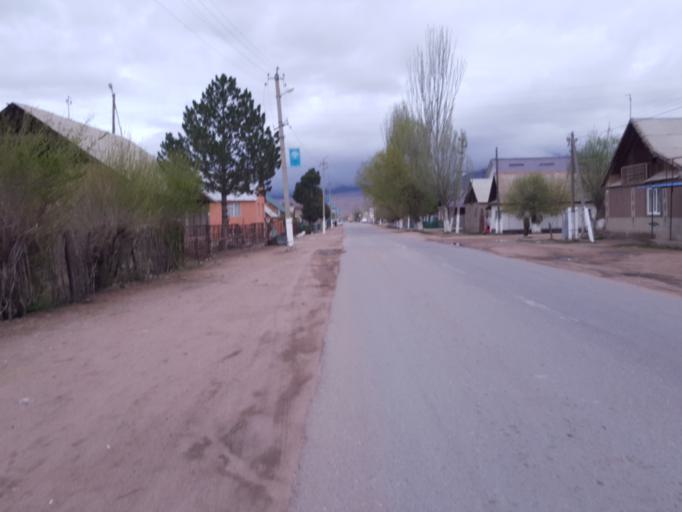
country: KG
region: Ysyk-Koel
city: Bokombayevskoye
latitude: 42.1153
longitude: 76.9868
